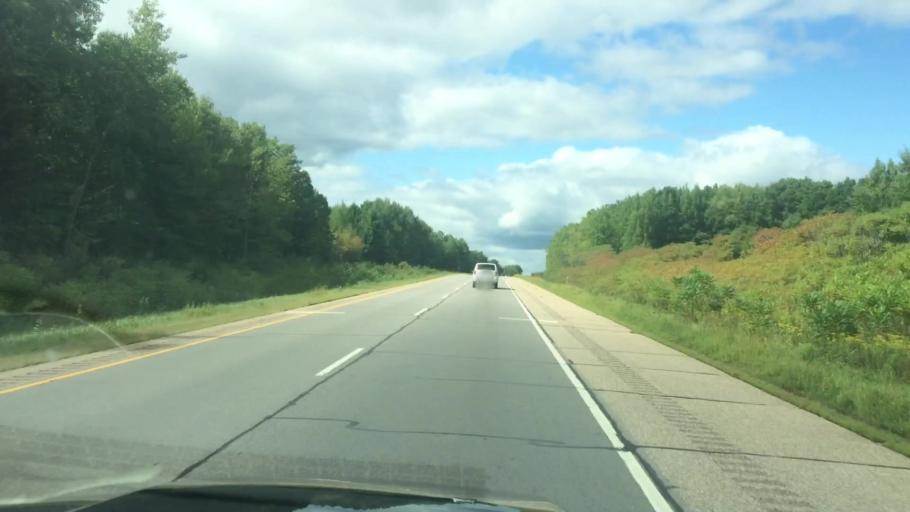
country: US
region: Wisconsin
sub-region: Marathon County
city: Mosinee
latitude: 44.6985
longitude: -89.6474
